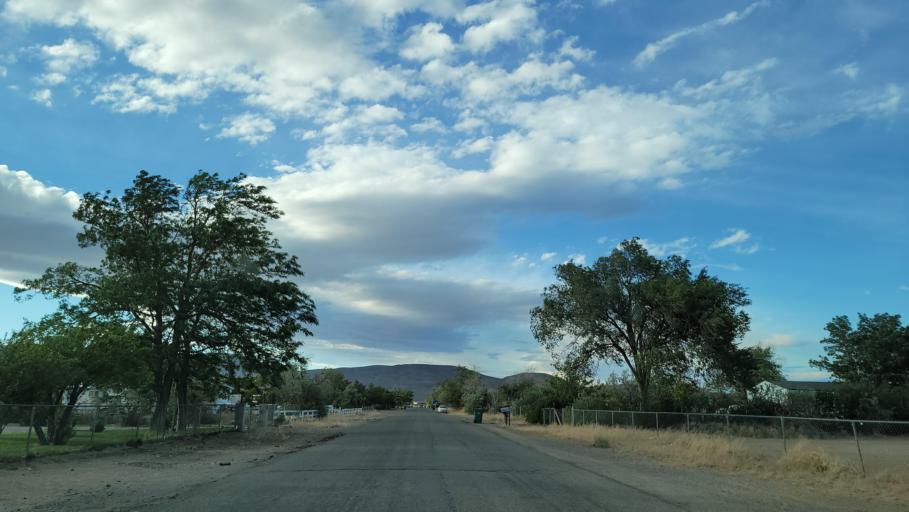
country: US
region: Nevada
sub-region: Lyon County
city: Silver Springs
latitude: 39.3929
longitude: -119.2374
